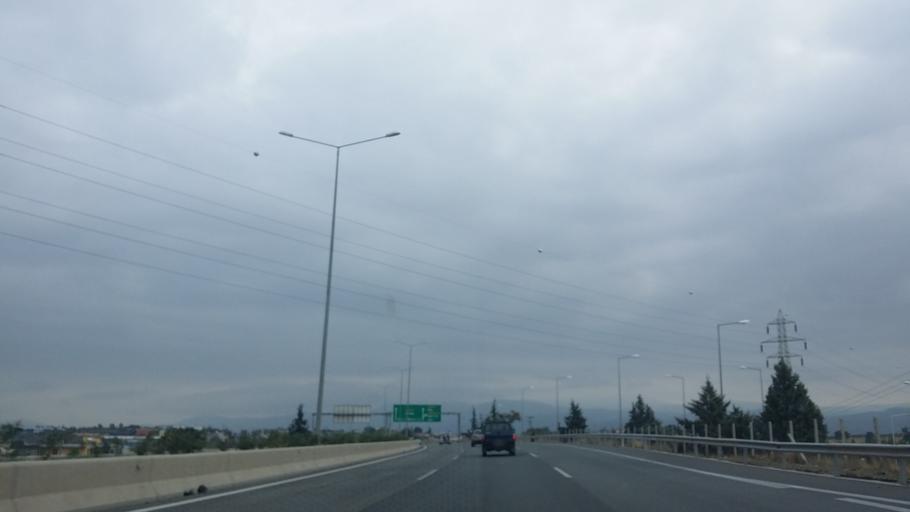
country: GR
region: Central Greece
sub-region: Nomos Voiotias
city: Schimatari
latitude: 38.3318
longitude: 23.6021
